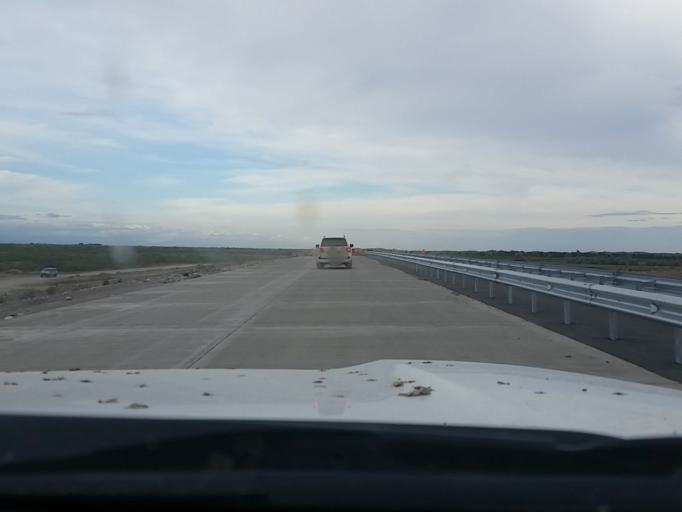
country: KZ
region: Almaty Oblysy
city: Zharkent
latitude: 44.1026
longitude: 80.0820
